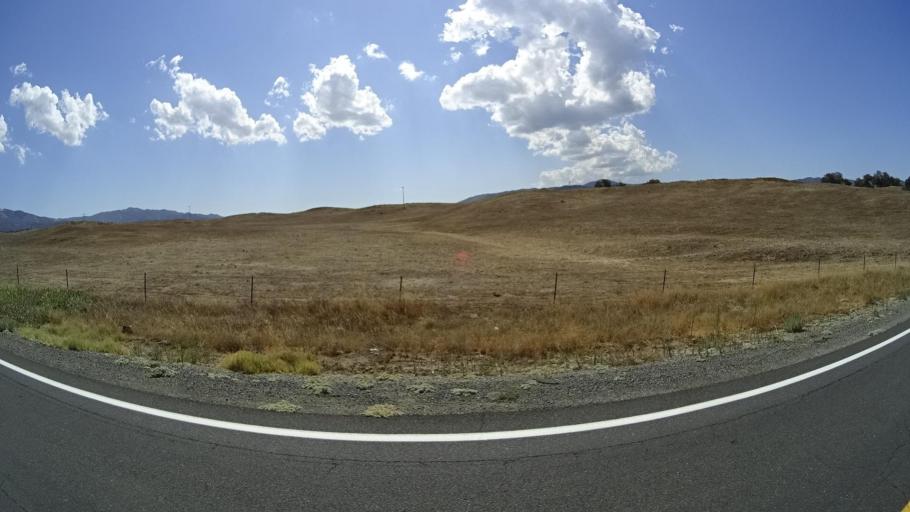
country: US
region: California
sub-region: San Diego County
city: Julian
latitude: 33.2610
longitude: -116.6632
